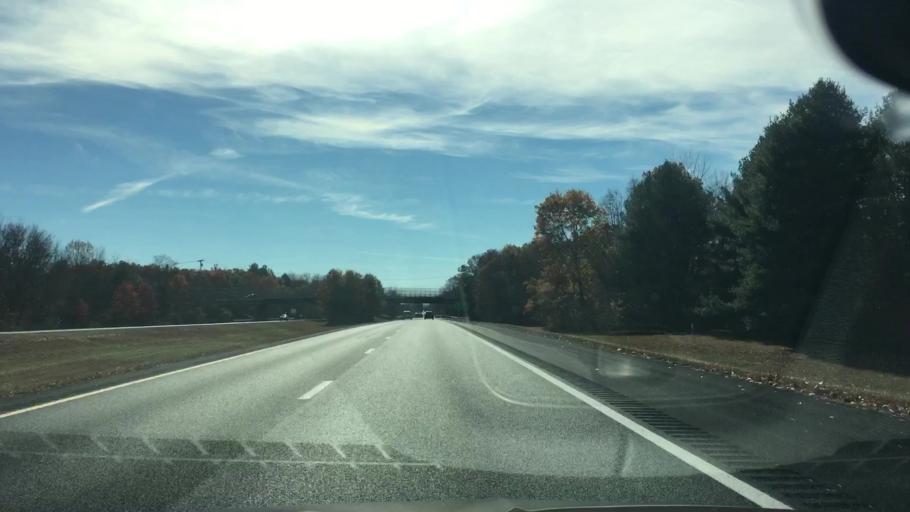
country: US
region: Massachusetts
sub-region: Franklin County
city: Whately
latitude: 42.4010
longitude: -72.6282
